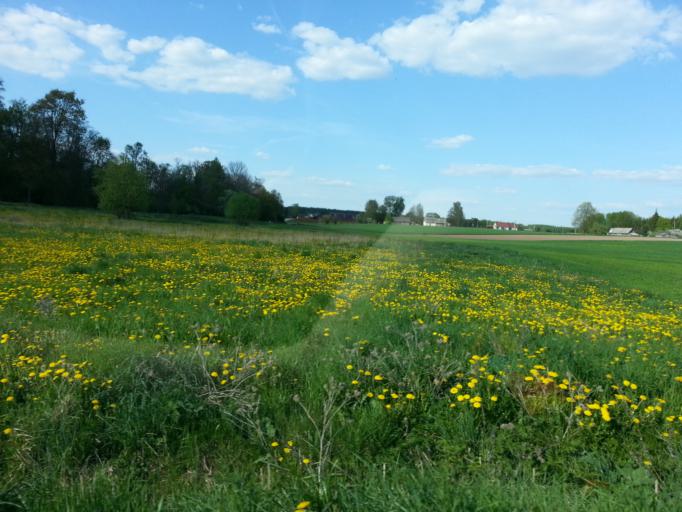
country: LT
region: Panevezys
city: Pasvalys
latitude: 56.0350
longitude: 24.3635
